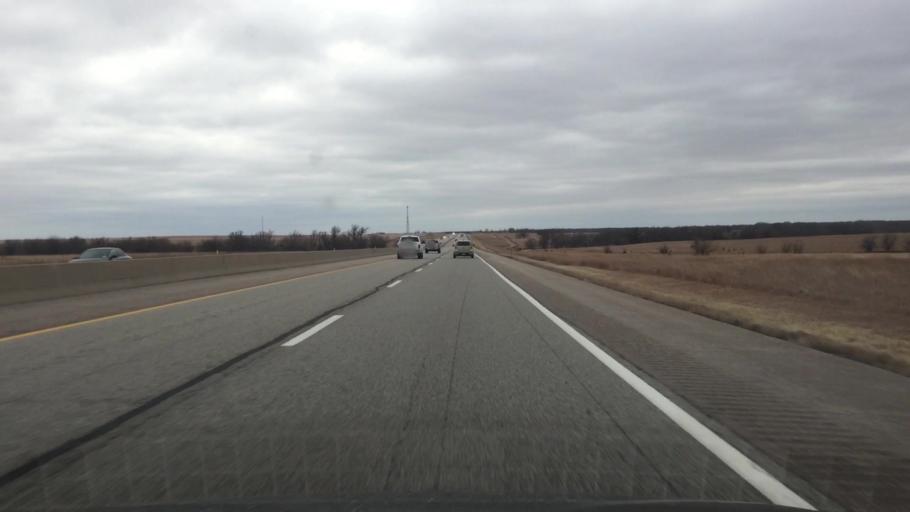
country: US
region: Kansas
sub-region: Butler County
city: El Dorado
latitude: 37.9751
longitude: -96.7173
